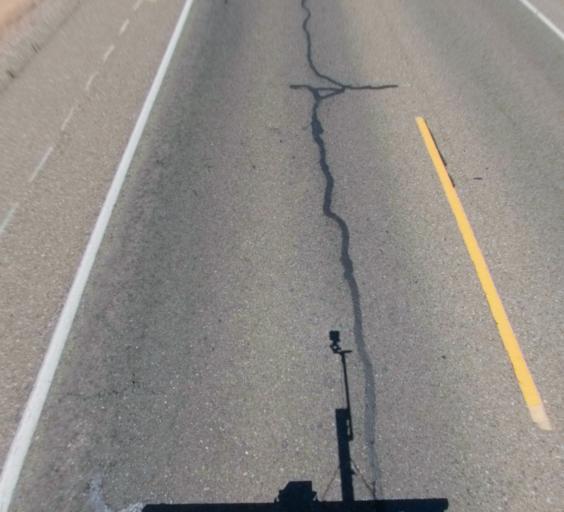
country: US
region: California
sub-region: Madera County
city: Bonadelle Ranchos-Madera Ranchos
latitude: 36.9230
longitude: -119.8274
